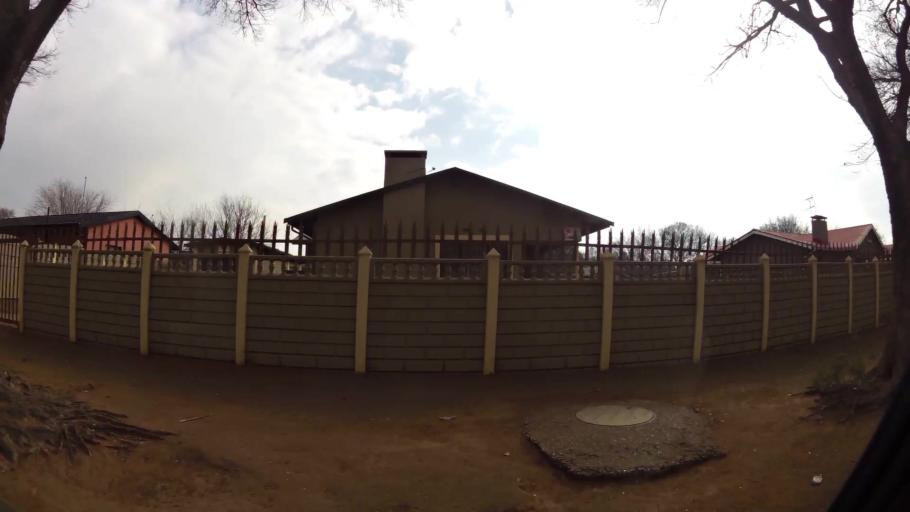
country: ZA
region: Gauteng
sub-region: Sedibeng District Municipality
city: Vanderbijlpark
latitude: -26.6794
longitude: 27.8343
